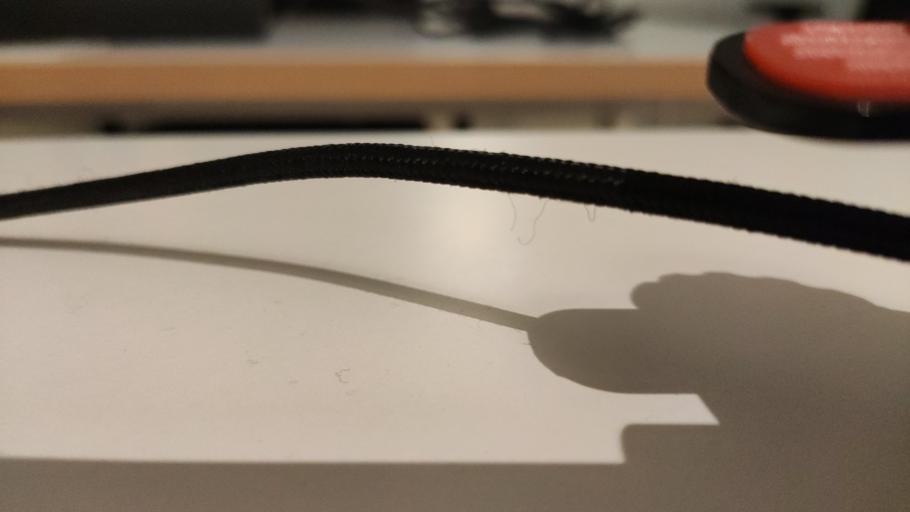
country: RU
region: Moskovskaya
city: Novosin'kovo
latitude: 56.3751
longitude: 37.3333
